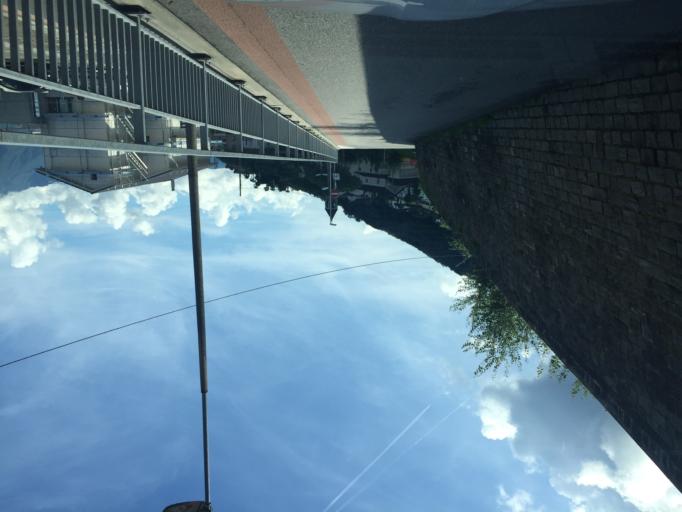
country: CH
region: Ticino
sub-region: Locarno District
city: Locarno
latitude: 46.1337
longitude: 8.8052
